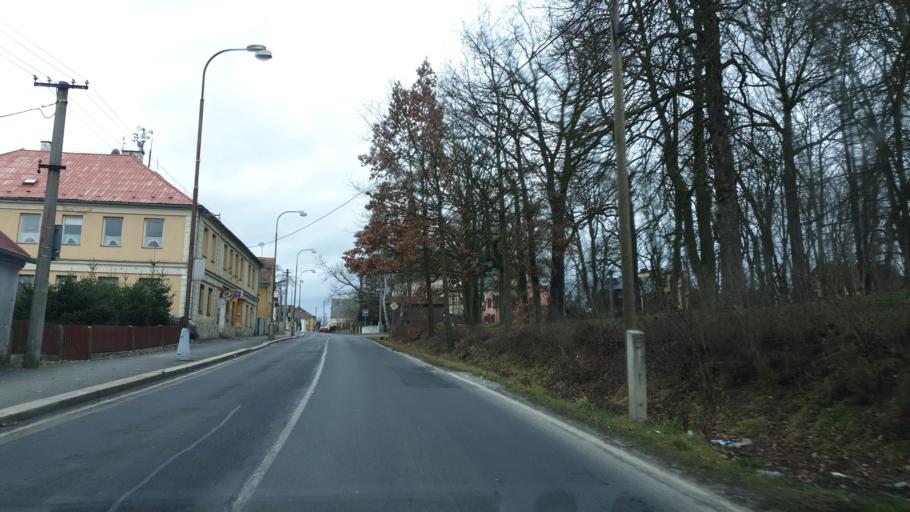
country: CZ
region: Karlovarsky
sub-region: Okres Cheb
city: Frantiskovy Lazne
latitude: 50.1287
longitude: 12.3452
